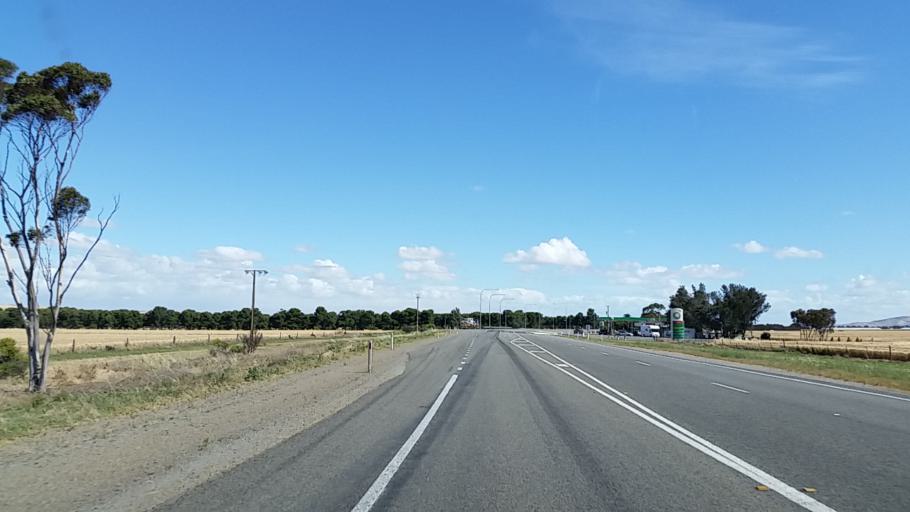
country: AU
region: South Australia
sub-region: Clare and Gilbert Valleys
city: Clare
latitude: -33.7710
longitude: 138.2124
